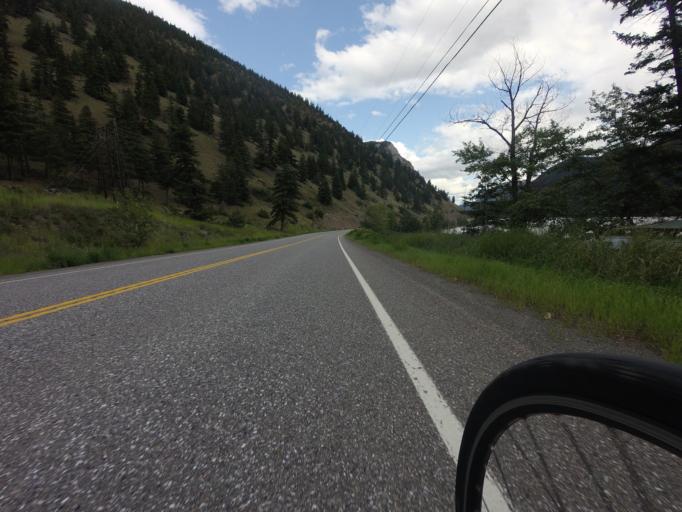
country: CA
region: British Columbia
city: Lillooet
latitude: 50.8716
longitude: -121.7411
